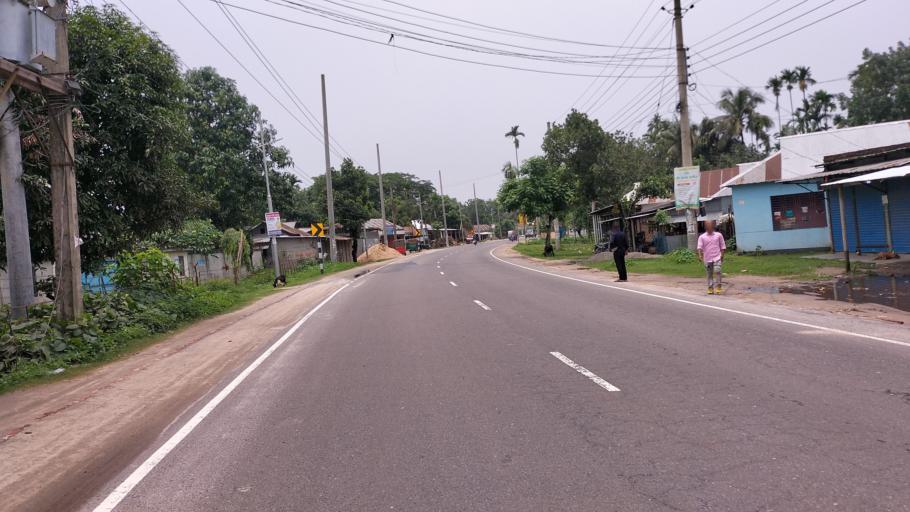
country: BD
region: Dhaka
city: Mymensingh
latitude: 24.7703
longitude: 90.4559
